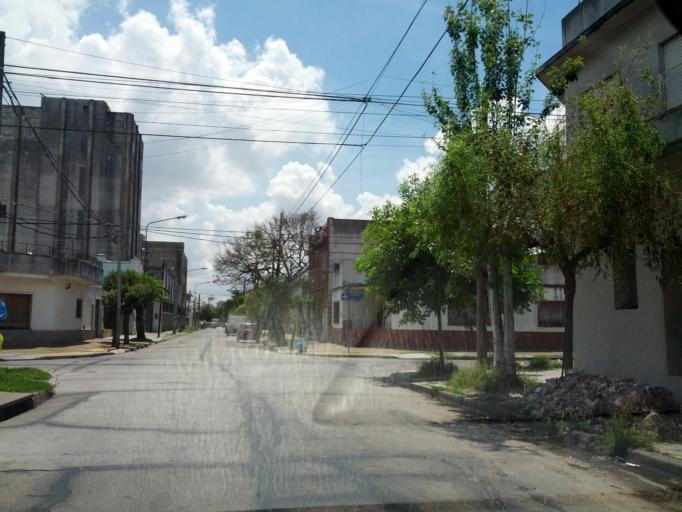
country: AR
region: Buenos Aires
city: San Justo
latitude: -34.6483
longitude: -58.5513
